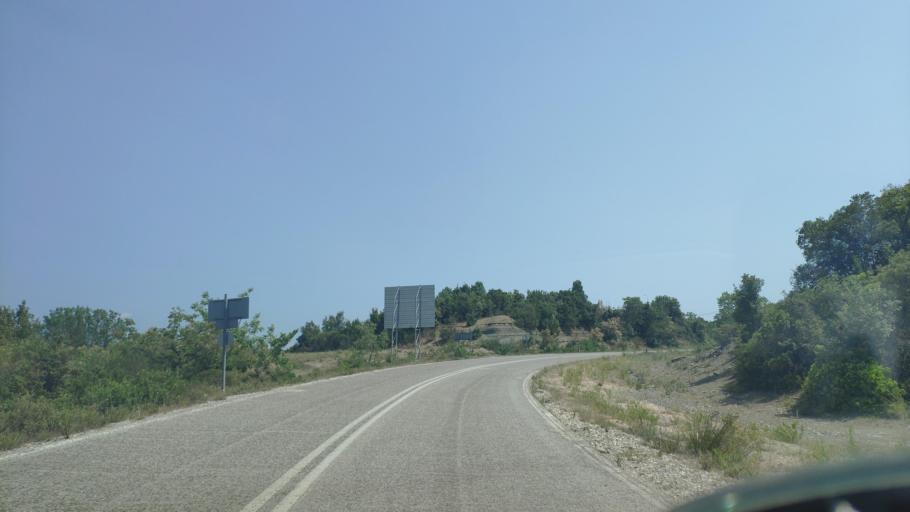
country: GR
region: Epirus
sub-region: Nomos Artas
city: Ano Kalentini
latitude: 39.2143
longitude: 21.1178
